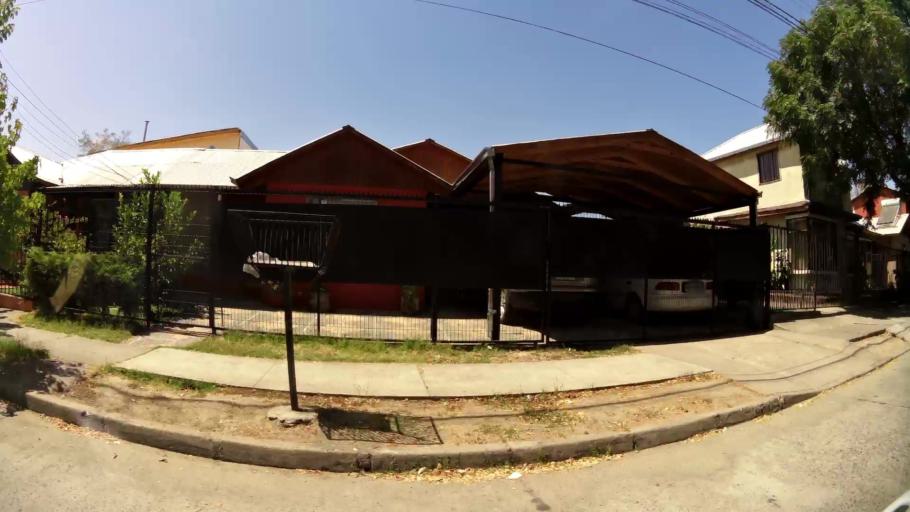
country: CL
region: Maule
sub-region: Provincia de Talca
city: Talca
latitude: -35.4288
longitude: -71.6312
